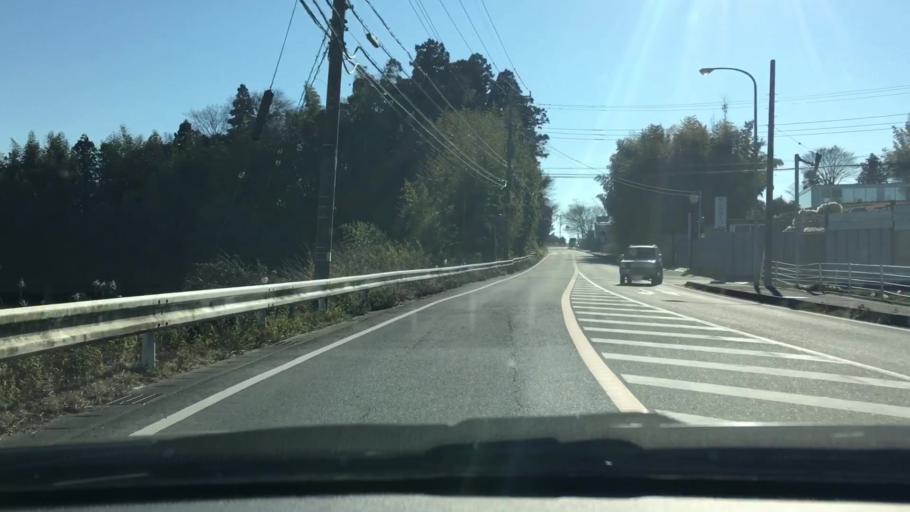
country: JP
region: Chiba
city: Shisui
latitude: 35.7120
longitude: 140.3168
